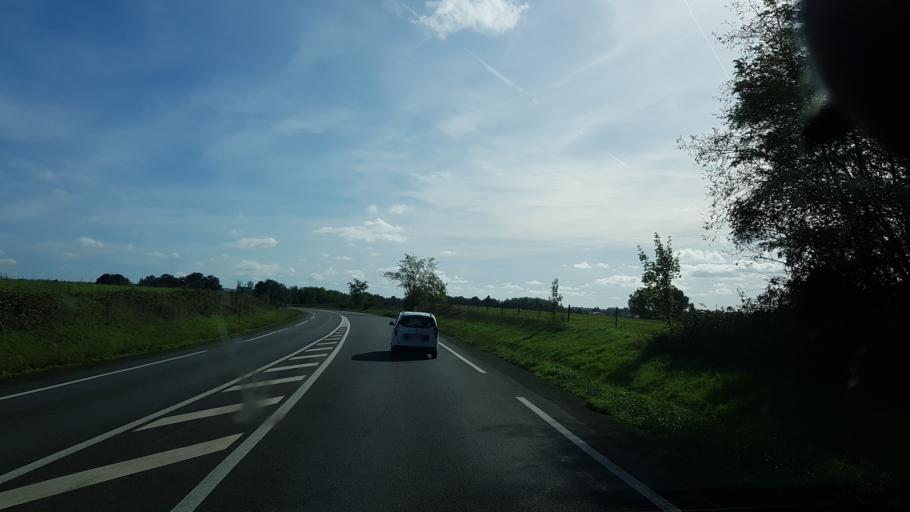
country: FR
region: Poitou-Charentes
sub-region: Departement de la Charente
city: Chasseneuil-sur-Bonnieure
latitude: 45.8429
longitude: 0.4605
